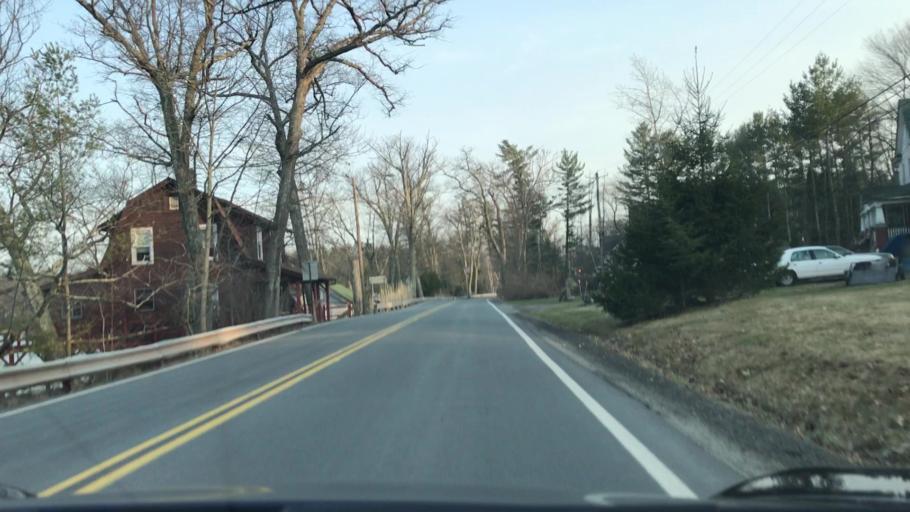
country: US
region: New York
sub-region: Sullivan County
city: Livingston Manor
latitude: 41.6816
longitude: -74.9939
